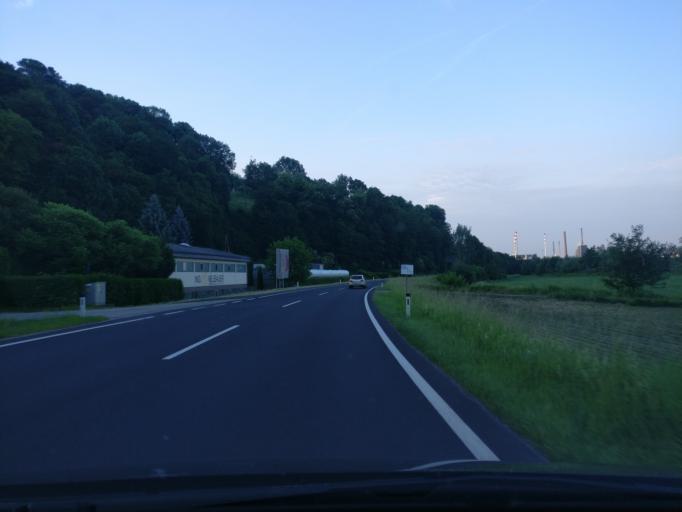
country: AT
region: Upper Austria
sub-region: Politischer Bezirk Urfahr-Umgebung
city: Steyregg
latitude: 48.2993
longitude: 14.3426
